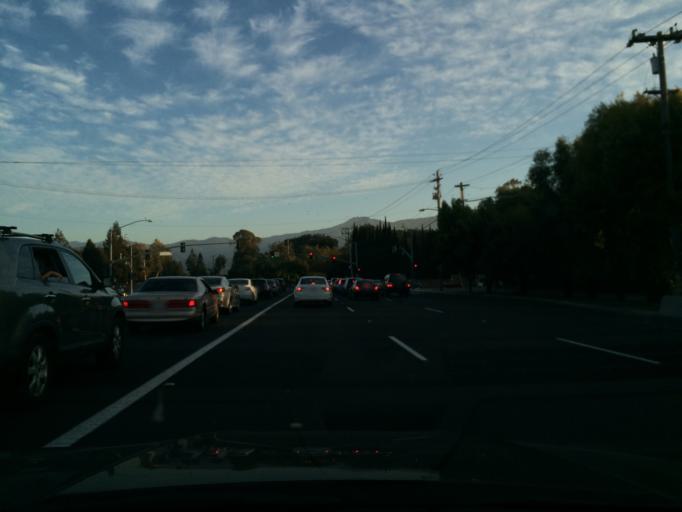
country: US
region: California
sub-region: Santa Clara County
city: Seven Trees
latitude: 37.2436
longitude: -121.8749
